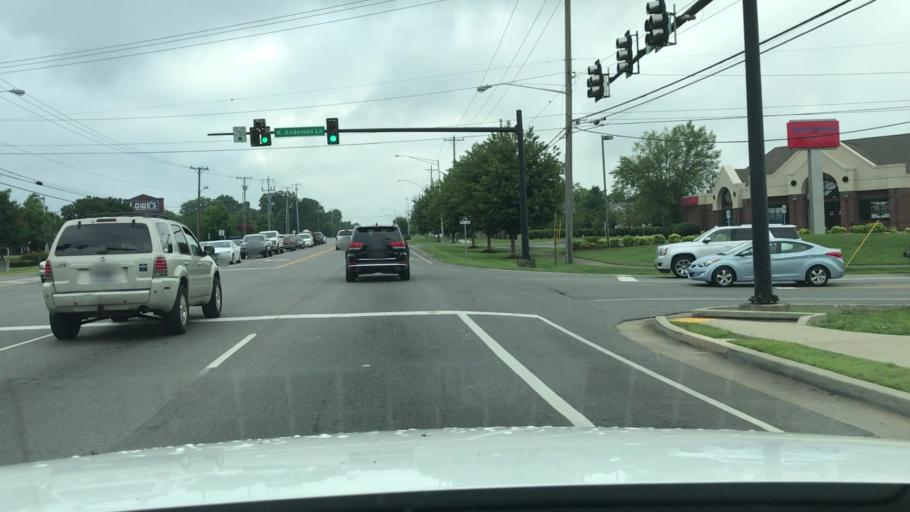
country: US
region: Tennessee
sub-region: Sumner County
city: Hendersonville
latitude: 36.3124
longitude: -86.5954
